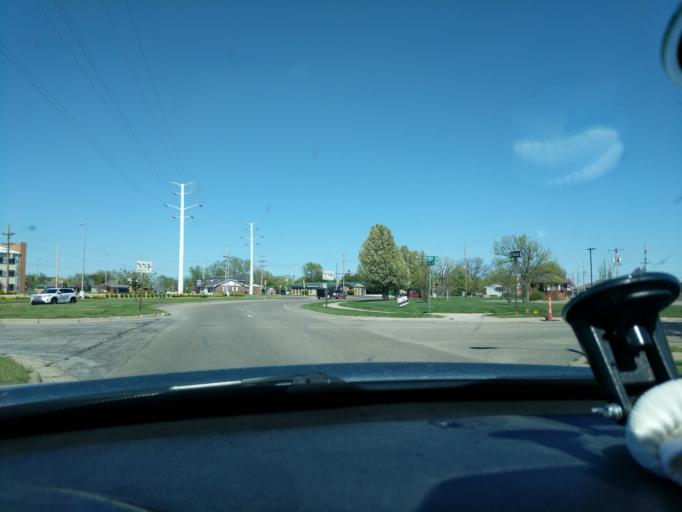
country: US
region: Kansas
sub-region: Saline County
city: Salina
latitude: 38.8045
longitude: -97.5958
